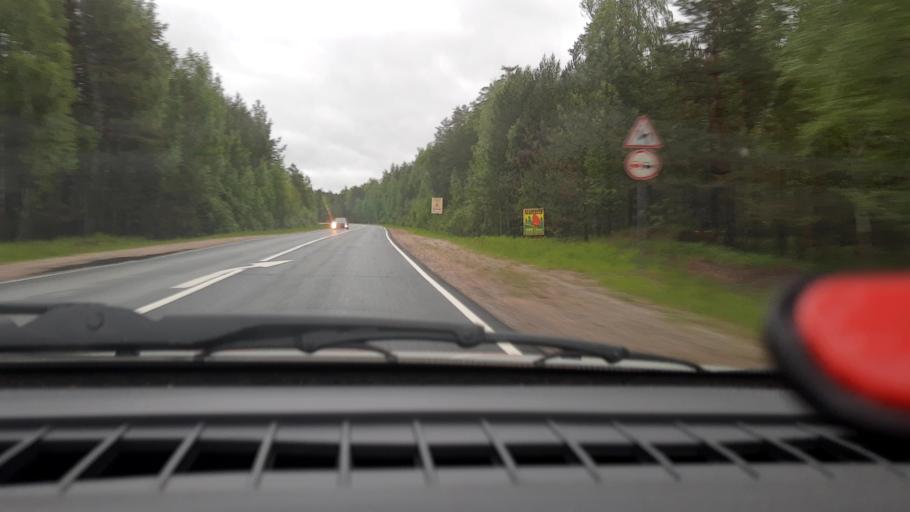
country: RU
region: Nizjnij Novgorod
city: Krasnyye Baki
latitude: 57.1724
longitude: 45.3214
